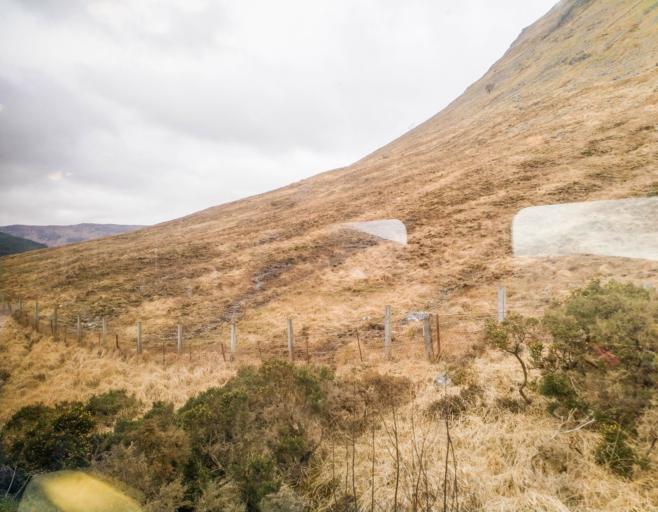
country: GB
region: Scotland
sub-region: Argyll and Bute
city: Garelochhead
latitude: 56.4874
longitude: -4.7173
